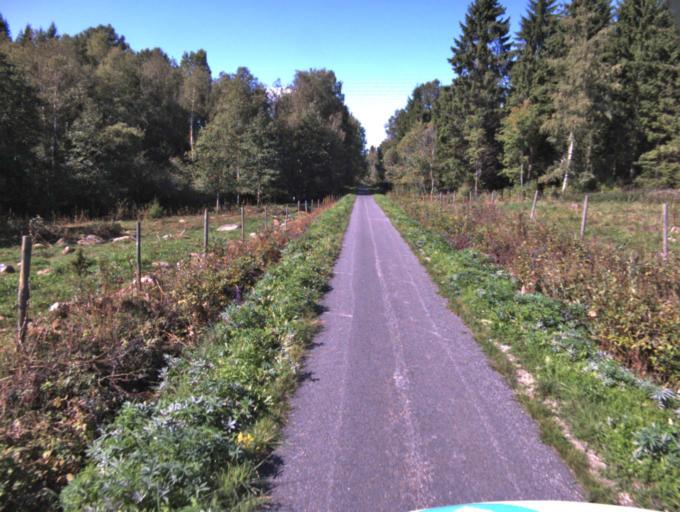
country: SE
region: Vaestra Goetaland
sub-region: Ulricehamns Kommun
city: Ulricehamn
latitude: 57.8040
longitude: 13.3631
